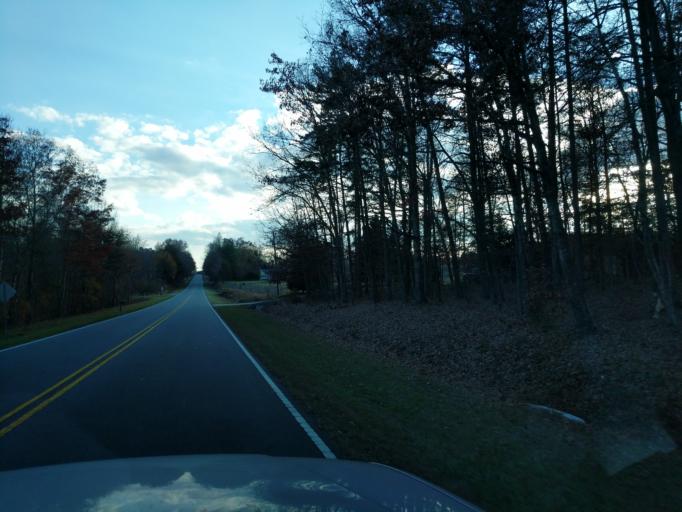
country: US
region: North Carolina
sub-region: Rutherford County
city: Rutherfordton
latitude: 35.4885
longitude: -81.9797
